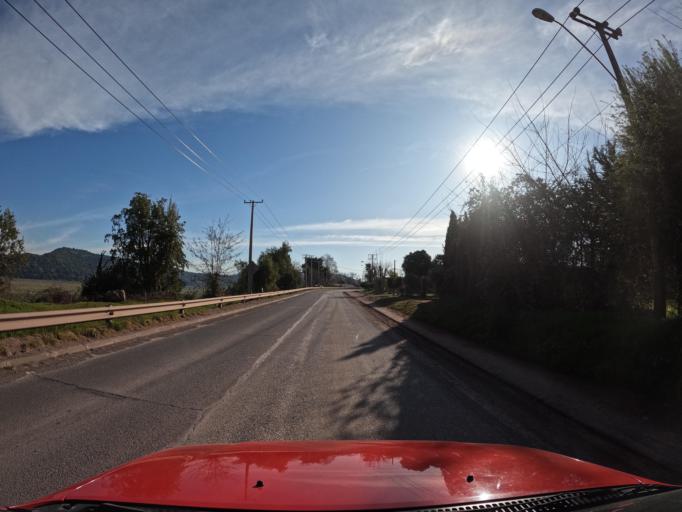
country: CL
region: Maule
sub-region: Provincia de Curico
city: Teno
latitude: -34.9620
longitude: -70.9663
